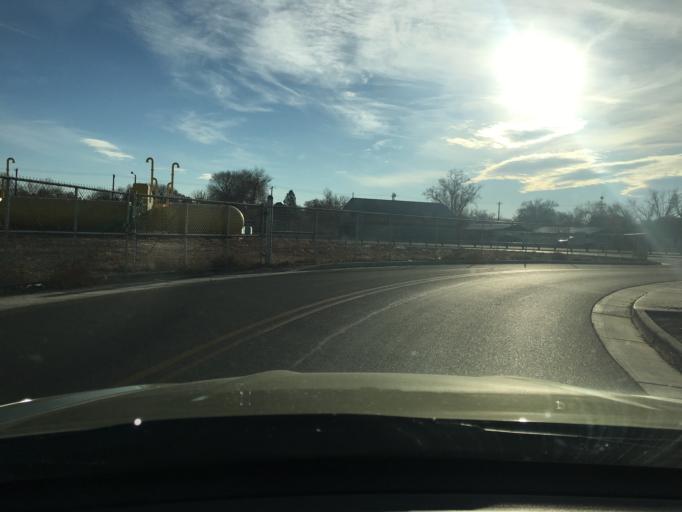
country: US
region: Colorado
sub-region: Delta County
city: Delta
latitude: 38.7429
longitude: -108.0772
